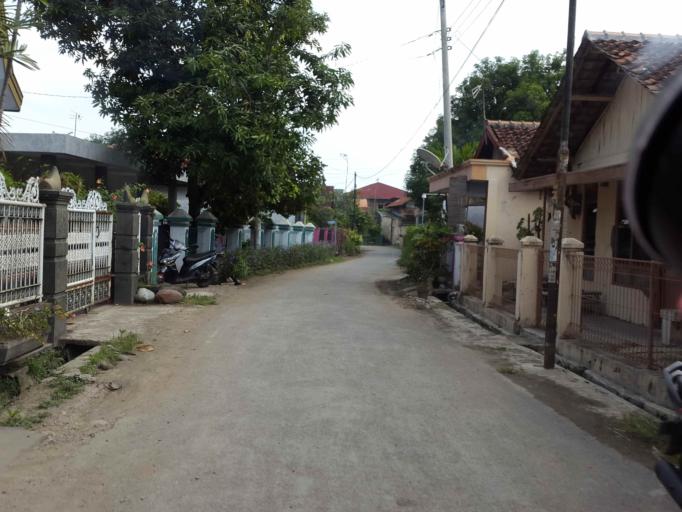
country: ID
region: Central Java
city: Pemalang
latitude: -6.9016
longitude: 109.3825
